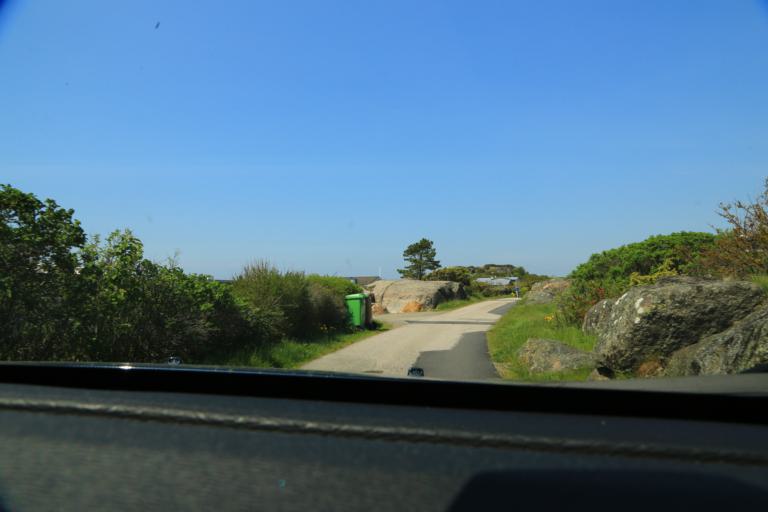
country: SE
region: Halland
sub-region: Varbergs Kommun
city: Varberg
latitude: 57.1421
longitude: 12.2171
